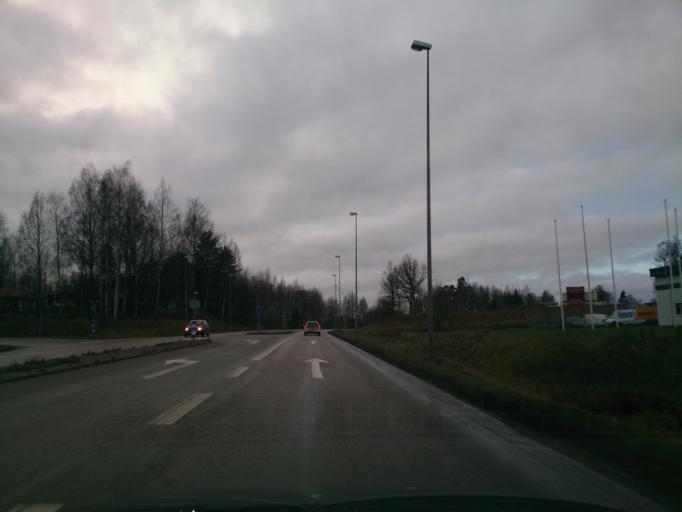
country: SE
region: OEstergoetland
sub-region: Atvidabergs Kommun
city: Atvidaberg
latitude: 58.2140
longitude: 15.9800
